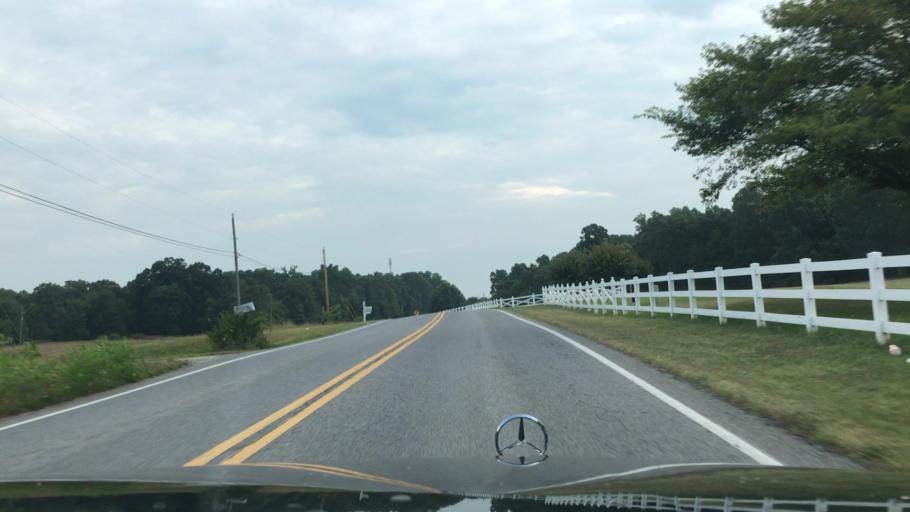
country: US
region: Virginia
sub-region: Campbell County
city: Timberlake
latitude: 37.3001
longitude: -79.3103
